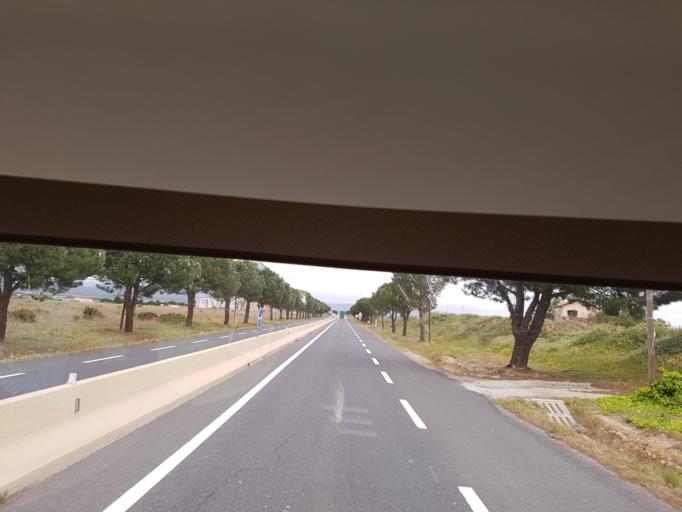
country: FR
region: Languedoc-Roussillon
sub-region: Departement des Pyrenees-Orientales
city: Rivesaltes
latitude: 42.7869
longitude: 2.9058
